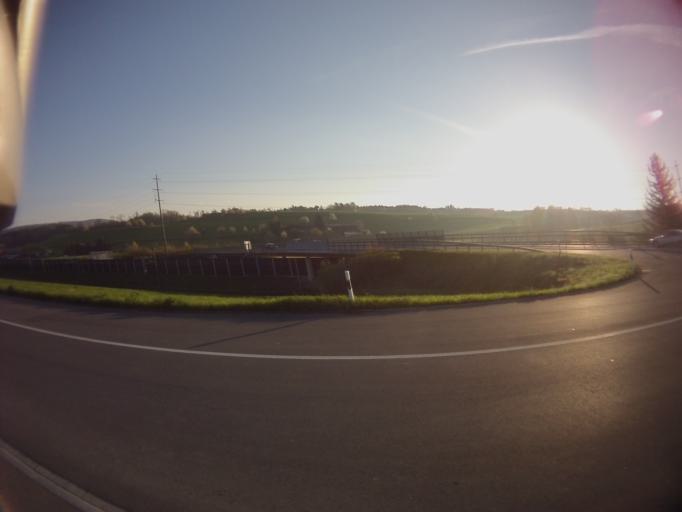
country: CH
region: Zurich
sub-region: Bezirk Affoltern
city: Knonau
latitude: 47.2157
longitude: 8.4683
